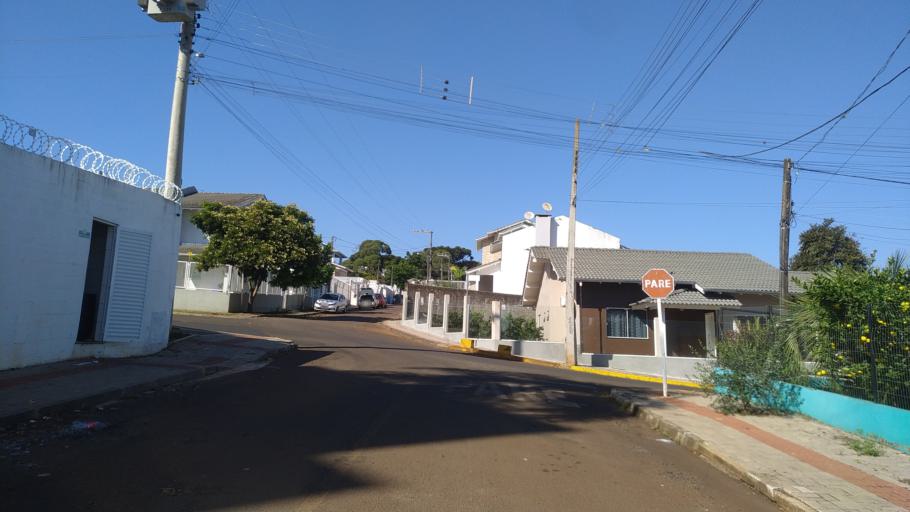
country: BR
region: Santa Catarina
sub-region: Chapeco
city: Chapeco
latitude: -27.0786
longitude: -52.6026
